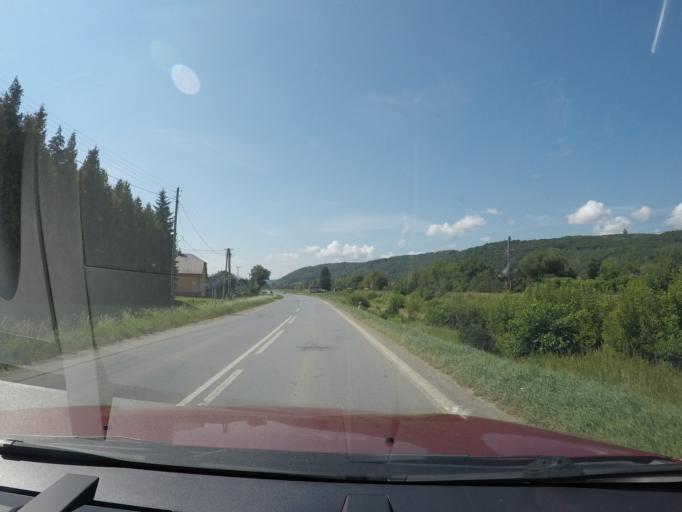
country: SK
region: Presovsky
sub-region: Okres Presov
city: Presov
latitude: 48.9592
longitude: 21.2417
